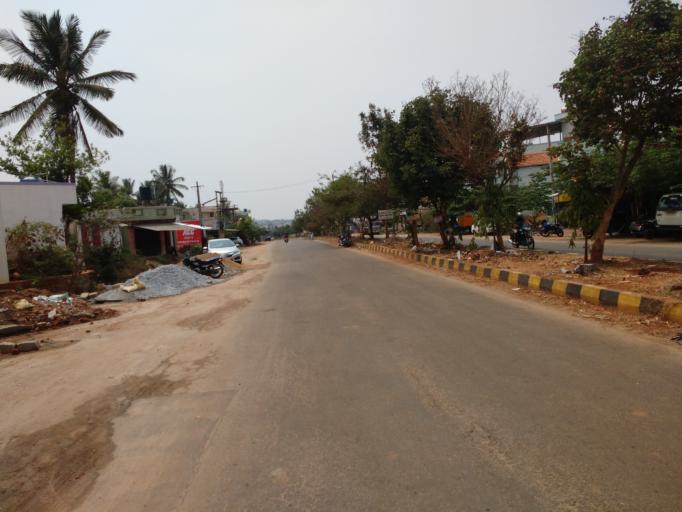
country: IN
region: Karnataka
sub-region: Hassan
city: Hassan
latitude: 13.0246
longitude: 76.1112
